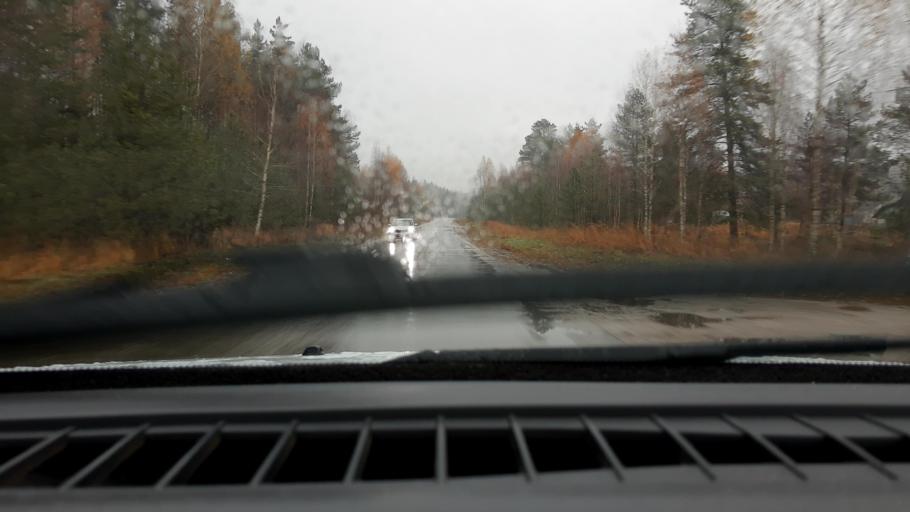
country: RU
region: Nizjnij Novgorod
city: Linda
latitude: 56.6935
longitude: 44.2044
